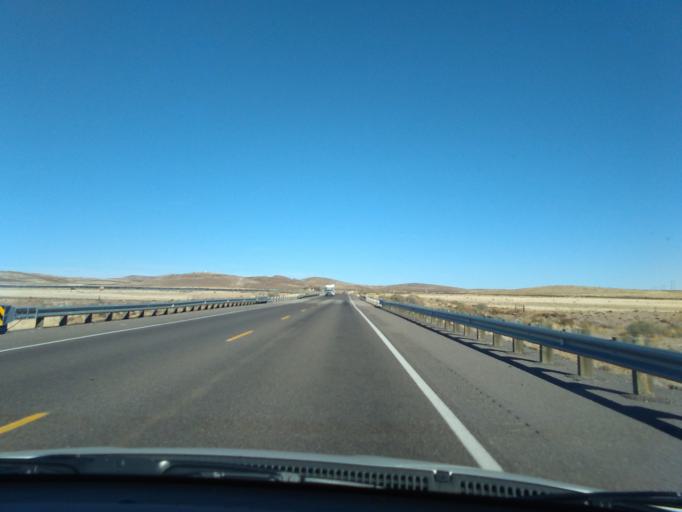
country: US
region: New Mexico
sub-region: Dona Ana County
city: Hatch
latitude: 32.5658
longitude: -107.4635
